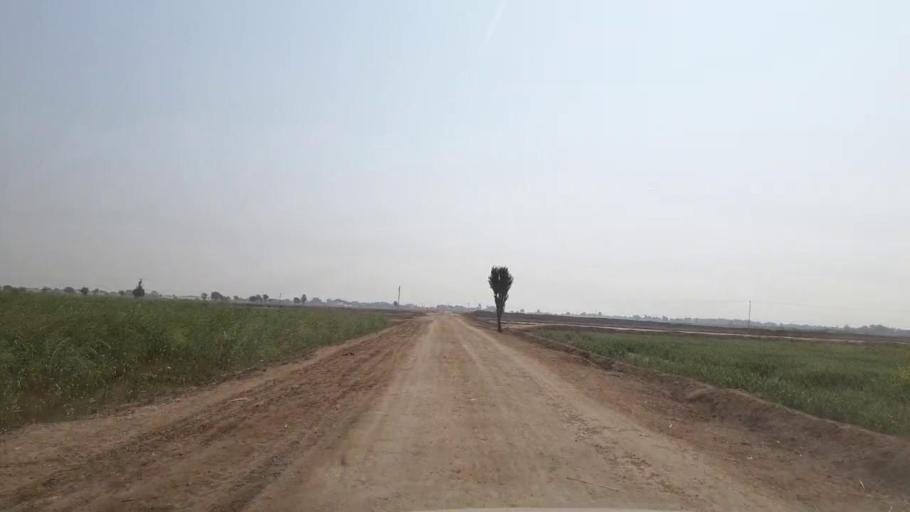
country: PK
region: Sindh
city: Mirpur Khas
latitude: 25.6459
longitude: 69.1400
